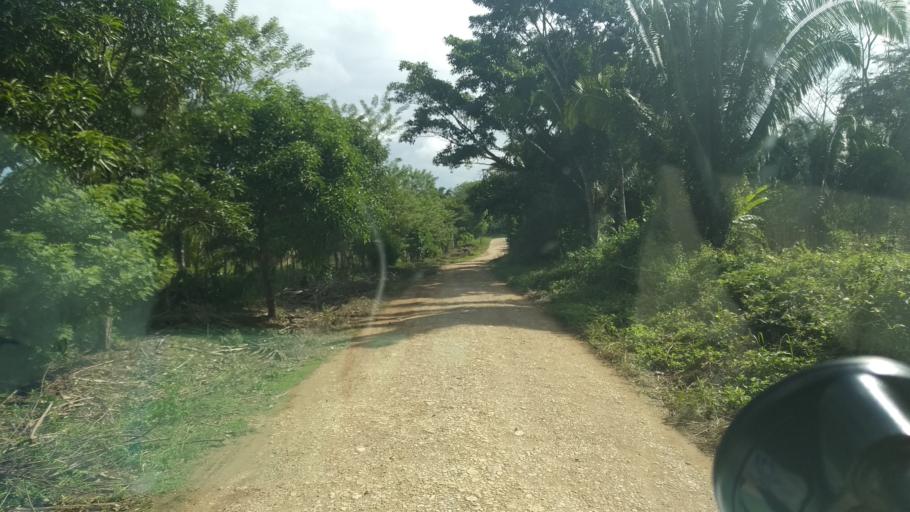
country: BZ
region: Toledo
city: Punta Gorda
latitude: 16.2073
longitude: -88.9166
